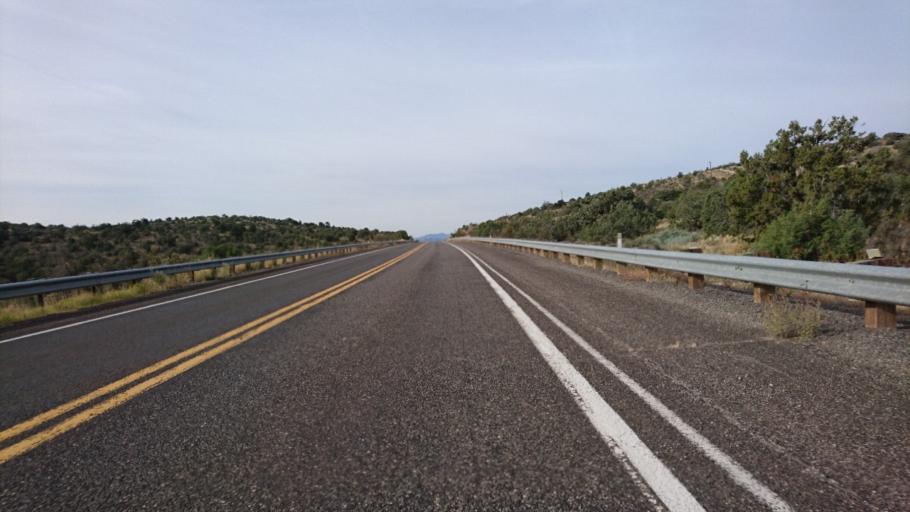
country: US
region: Arizona
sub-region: Mohave County
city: Peach Springs
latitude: 35.5500
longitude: -113.3934
